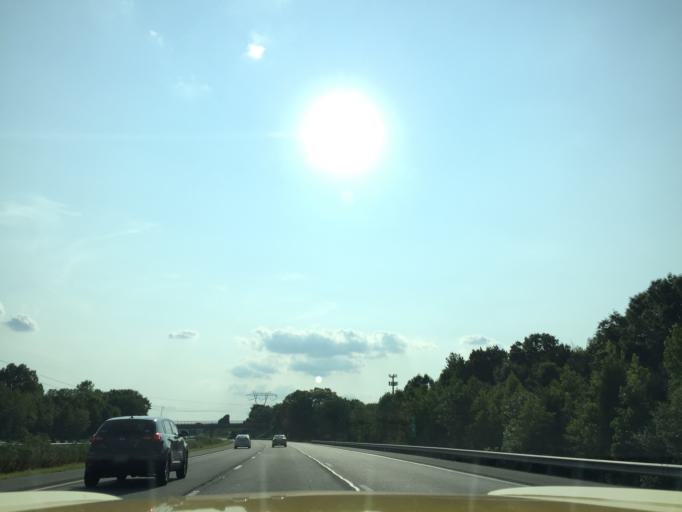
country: US
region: Maryland
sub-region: Cecil County
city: Elkton
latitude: 39.6465
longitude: -75.8435
